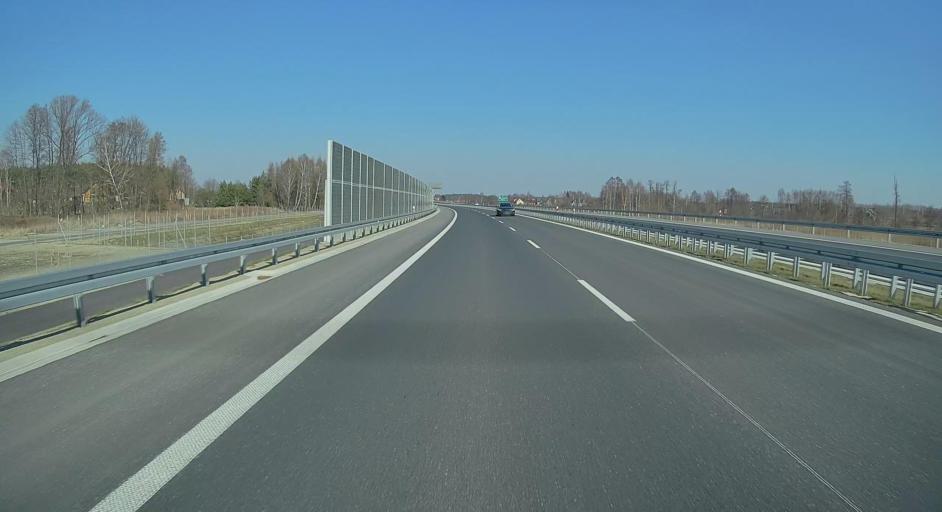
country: PL
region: Subcarpathian Voivodeship
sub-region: Powiat lezajski
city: Letownia
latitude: 50.3394
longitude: 22.2011
